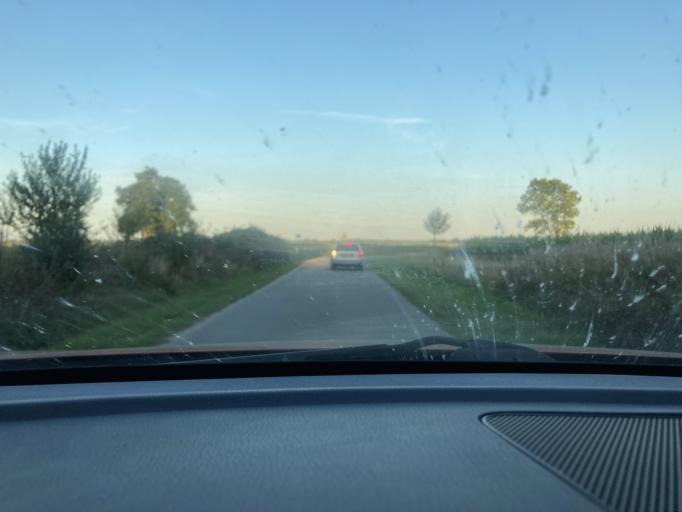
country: DE
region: Mecklenburg-Vorpommern
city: Alt-Sanitz
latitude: 53.7263
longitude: 13.6587
